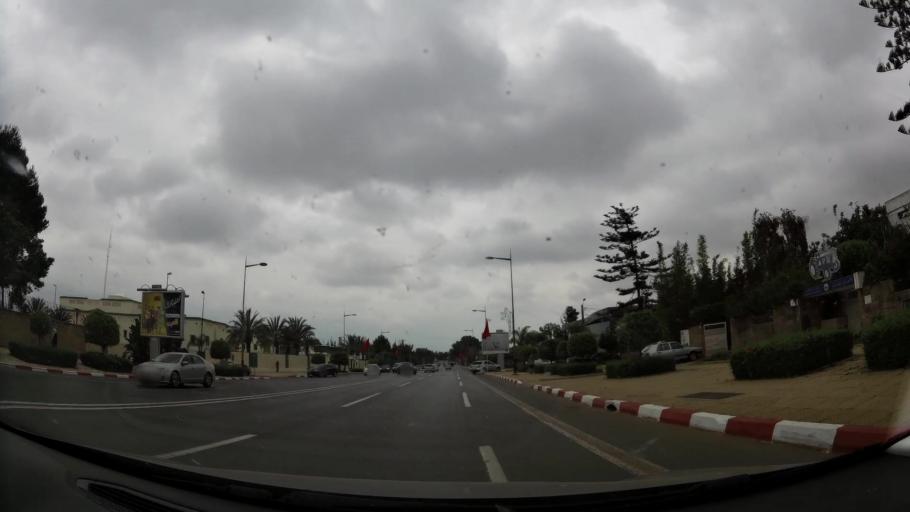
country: MA
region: Rabat-Sale-Zemmour-Zaer
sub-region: Rabat
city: Rabat
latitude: 33.9707
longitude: -6.8290
